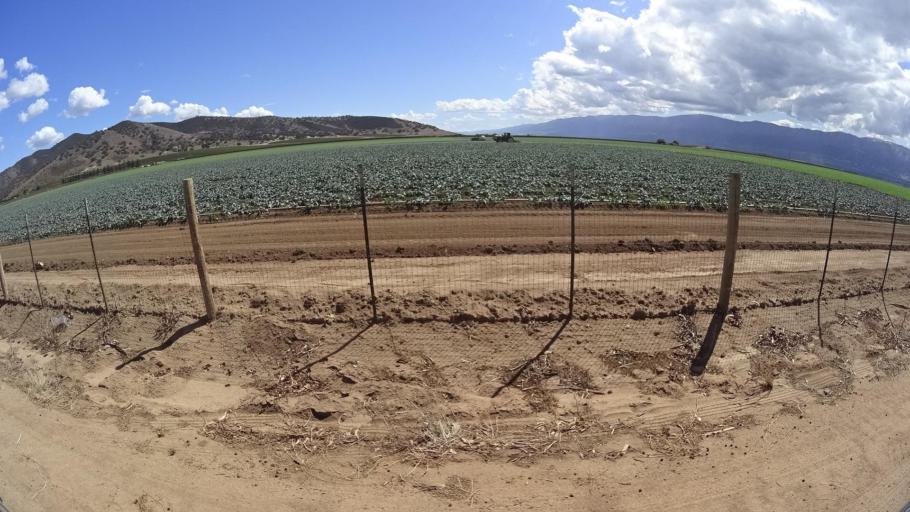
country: US
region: California
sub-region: Monterey County
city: Chualar
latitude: 36.5888
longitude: -121.4647
